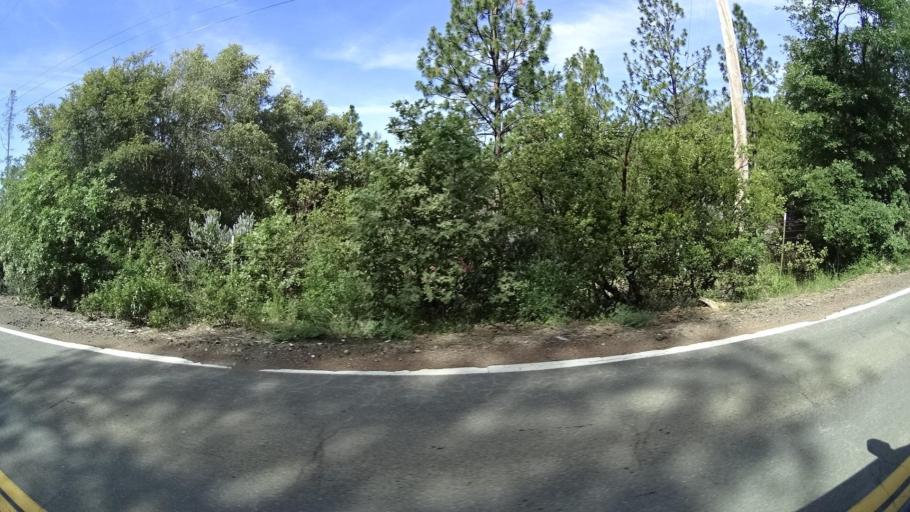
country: US
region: California
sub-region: Lake County
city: Cobb
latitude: 38.8837
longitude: -122.7846
